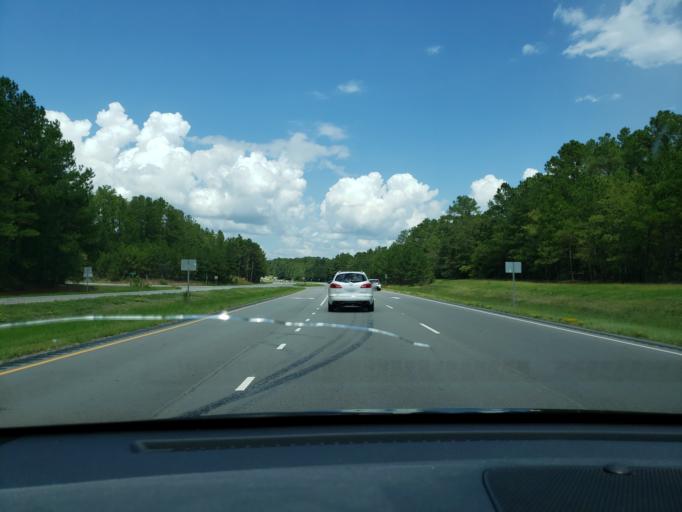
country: US
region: North Carolina
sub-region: Robeson County
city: Saint Pauls
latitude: 34.8538
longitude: -78.8504
